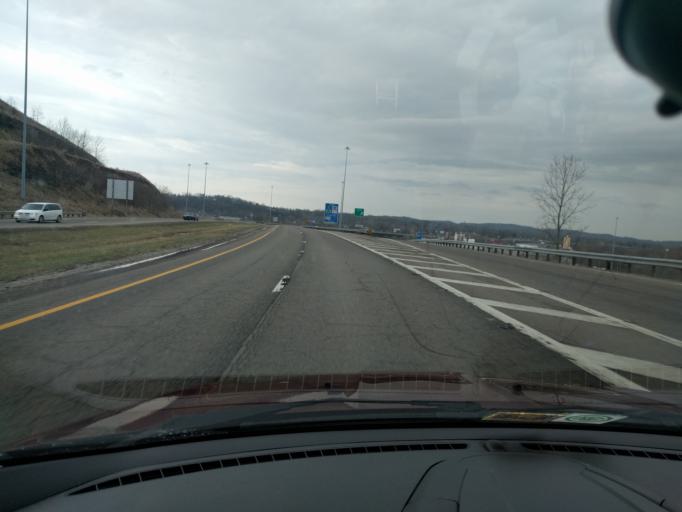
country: US
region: West Virginia
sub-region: Wood County
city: Parkersburg
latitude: 39.2601
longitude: -81.5293
